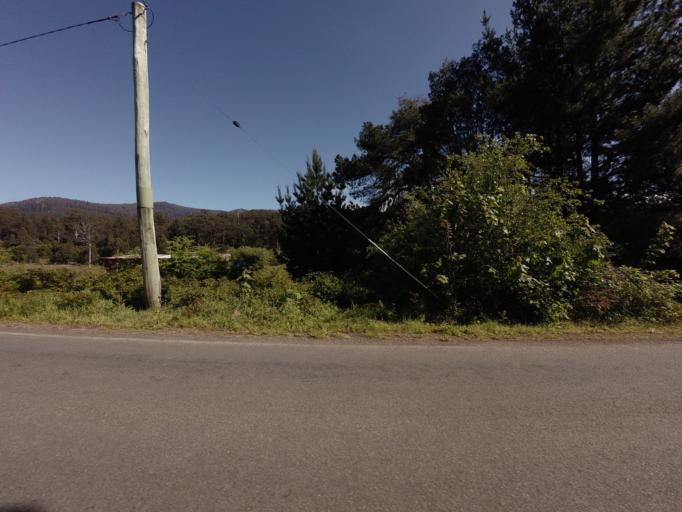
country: AU
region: Tasmania
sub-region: Derwent Valley
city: New Norfolk
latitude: -42.7120
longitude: 146.7031
